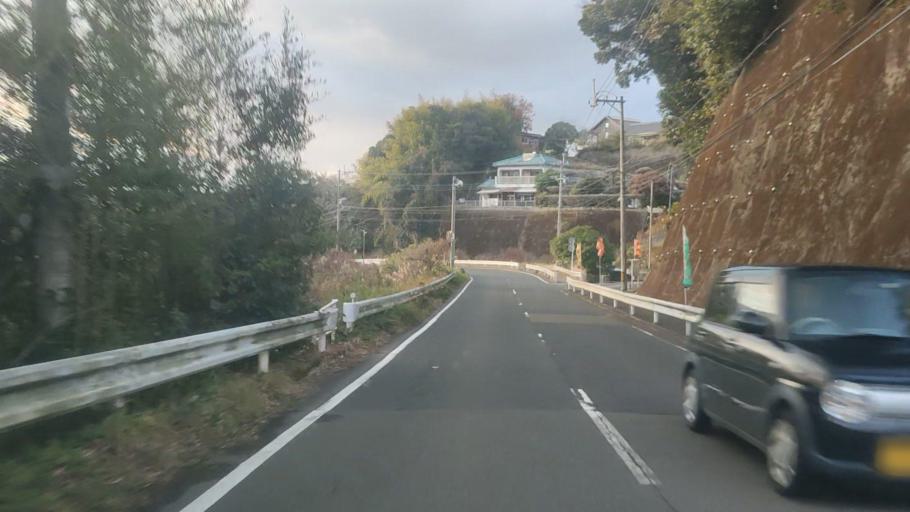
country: JP
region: Kagoshima
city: Kagoshima-shi
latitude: 31.6271
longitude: 130.5516
